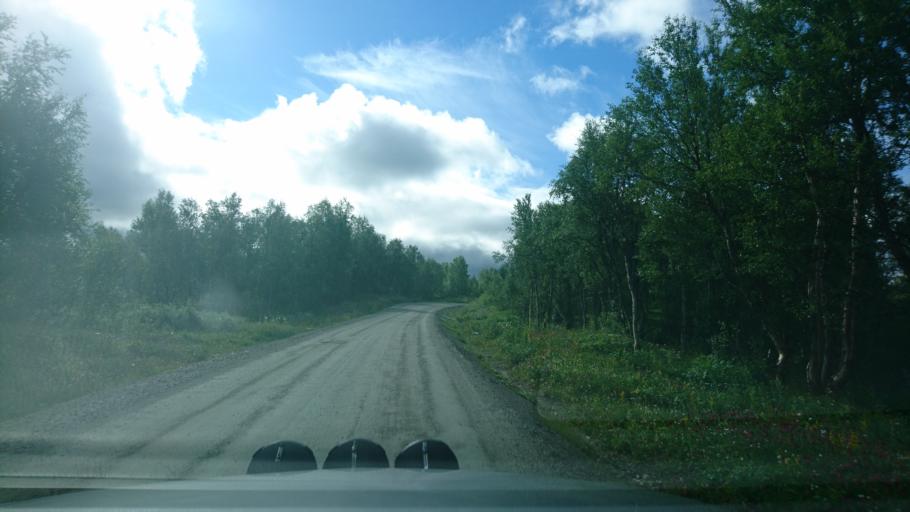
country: NO
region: Nordland
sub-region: Hattfjelldal
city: Hattfjelldal
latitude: 65.7108
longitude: 15.0980
